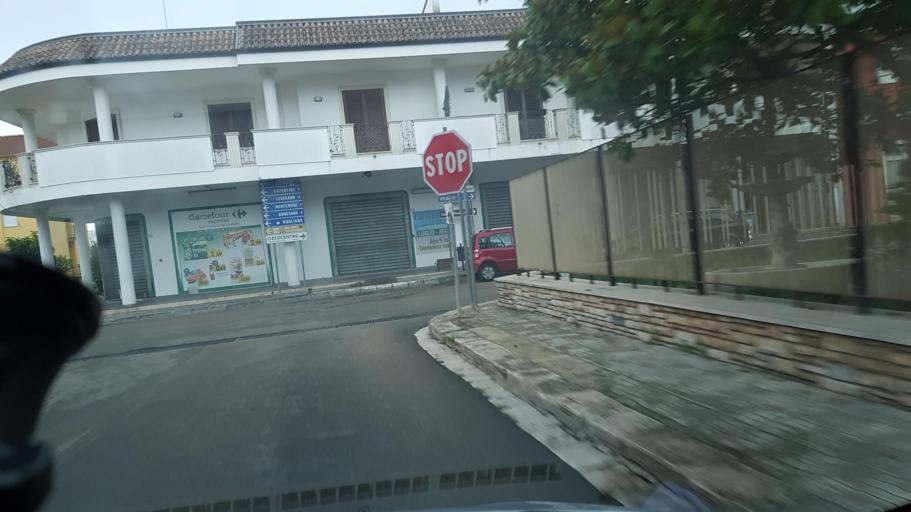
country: IT
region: Apulia
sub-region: Provincia di Lecce
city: Carmiano
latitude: 40.3453
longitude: 18.0390
